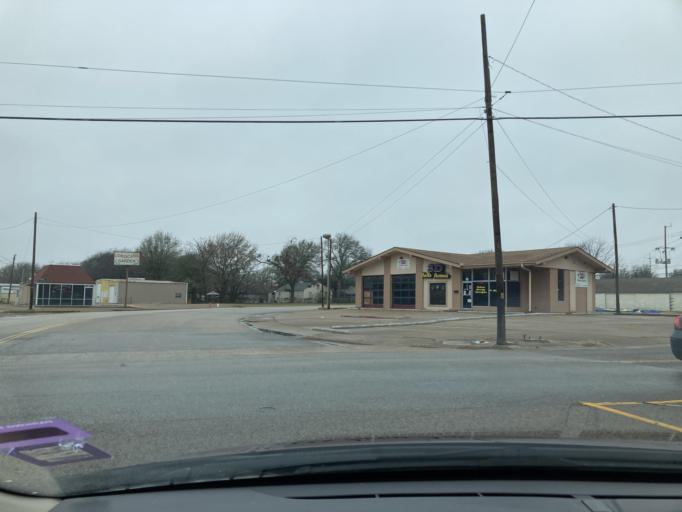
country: US
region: Texas
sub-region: Navarro County
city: Corsicana
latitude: 32.1057
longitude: -96.4735
